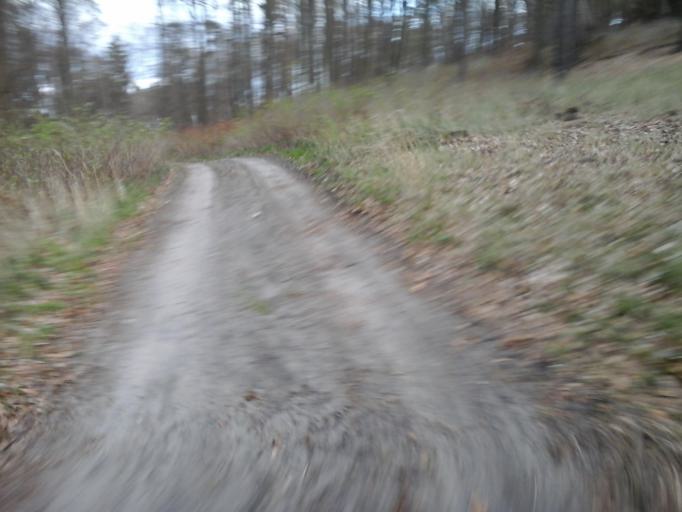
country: PL
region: West Pomeranian Voivodeship
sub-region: Powiat choszczenski
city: Bierzwnik
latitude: 53.0365
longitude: 15.5983
